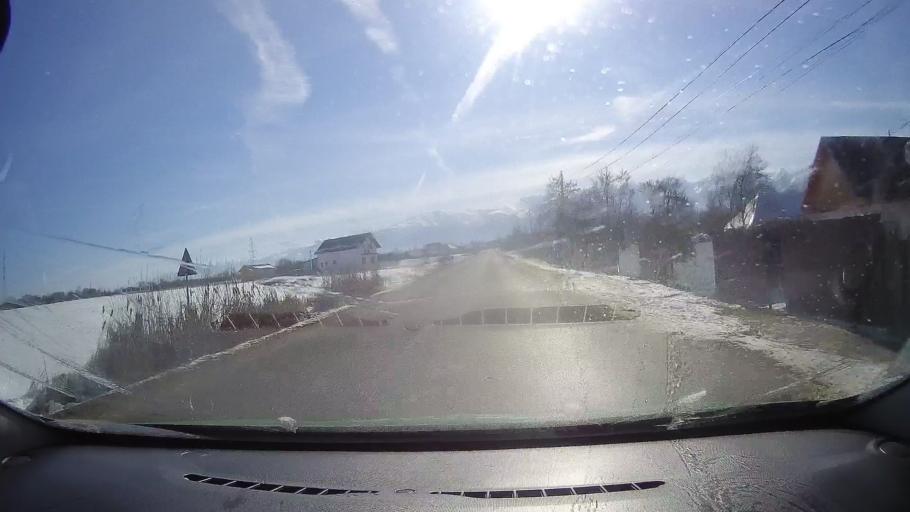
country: RO
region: Brasov
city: Ucea de Sus
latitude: 45.7534
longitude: 24.6908
